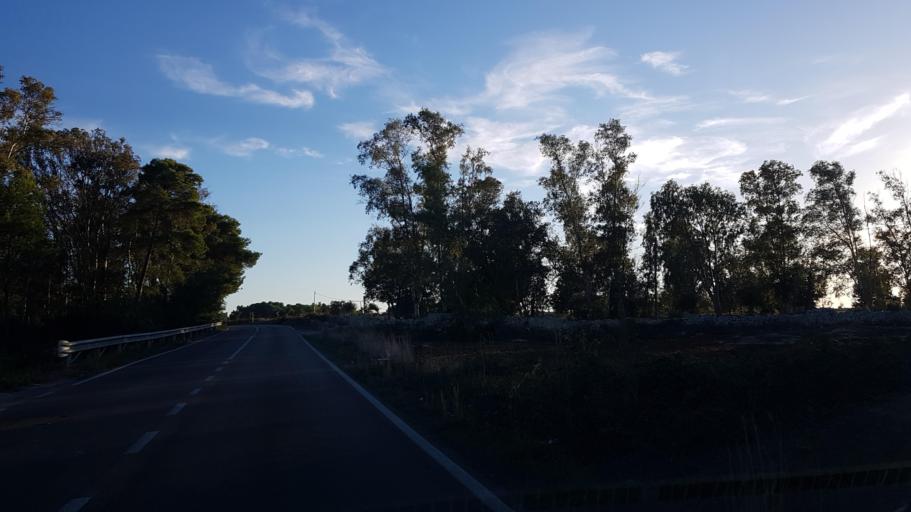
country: IT
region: Apulia
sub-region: Provincia di Lecce
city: Giorgilorio
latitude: 40.4039
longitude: 18.1974
